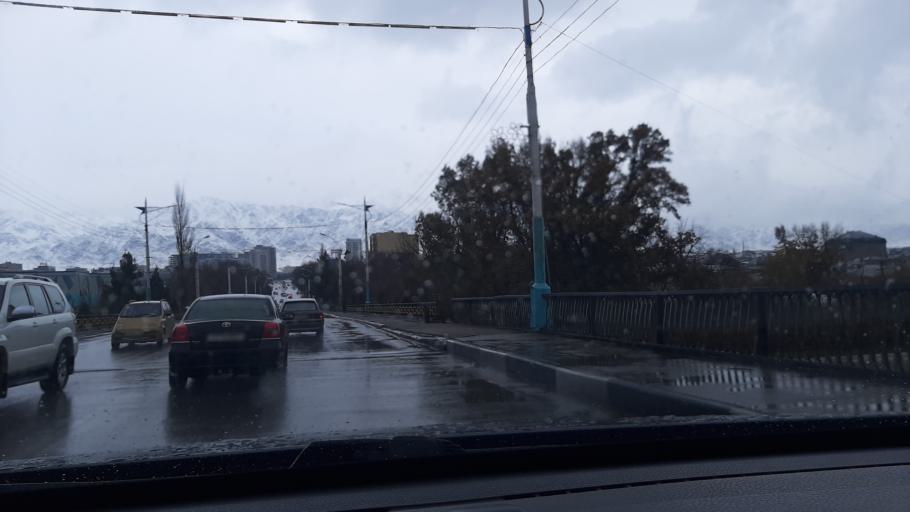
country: TJ
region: Viloyati Sughd
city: Khujand
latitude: 40.2912
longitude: 69.6197
